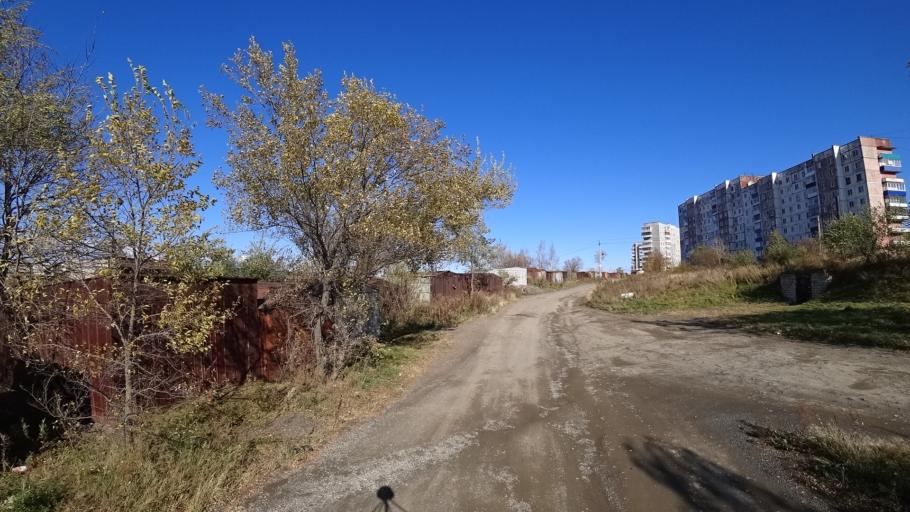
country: RU
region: Khabarovsk Krai
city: Amursk
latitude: 50.2177
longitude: 136.8900
